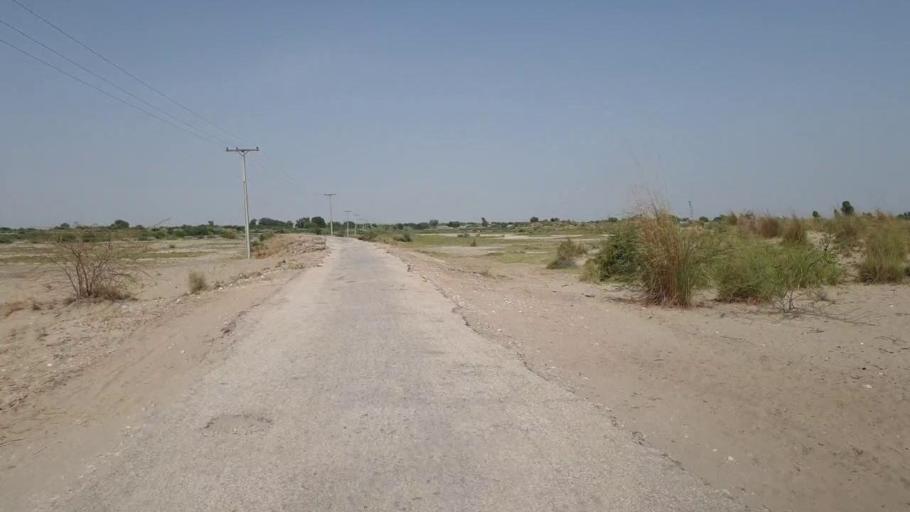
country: PK
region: Sindh
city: Jam Sahib
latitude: 26.4087
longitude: 68.8994
